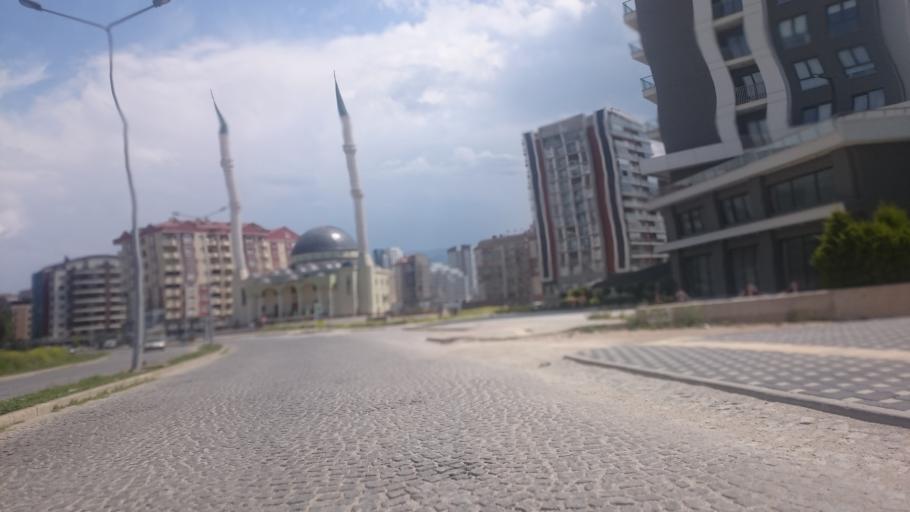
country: TR
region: Bursa
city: Cali
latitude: 40.2230
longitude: 28.9423
